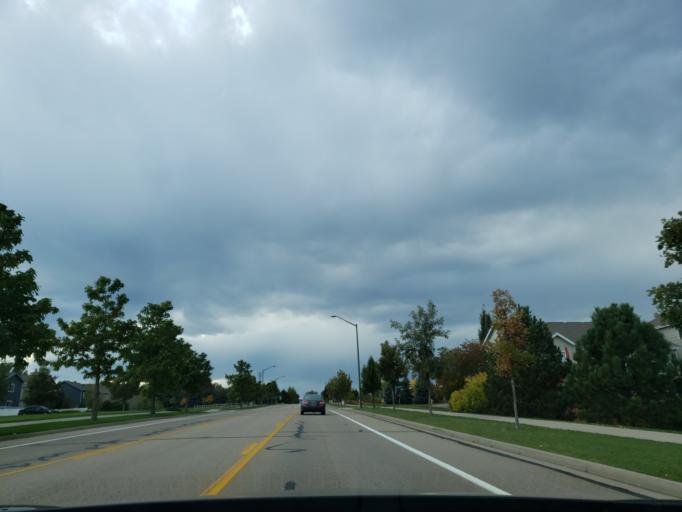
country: US
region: Colorado
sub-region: Larimer County
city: Fort Collins
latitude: 40.6248
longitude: -105.0360
